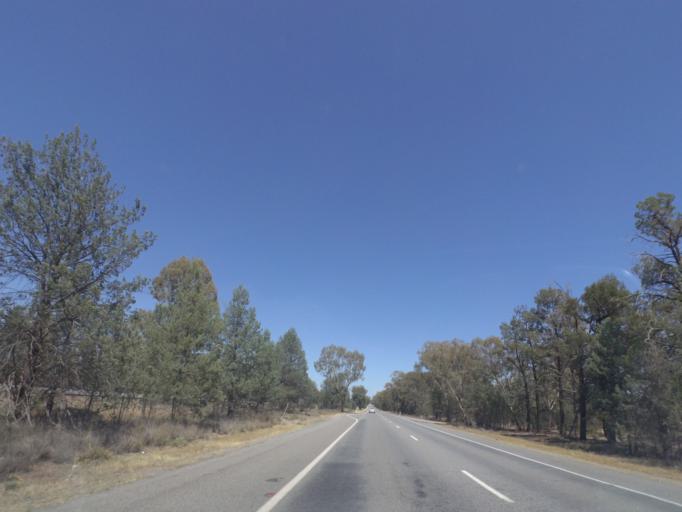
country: AU
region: New South Wales
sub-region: Narrandera
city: Narrandera
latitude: -34.7369
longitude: 146.5918
